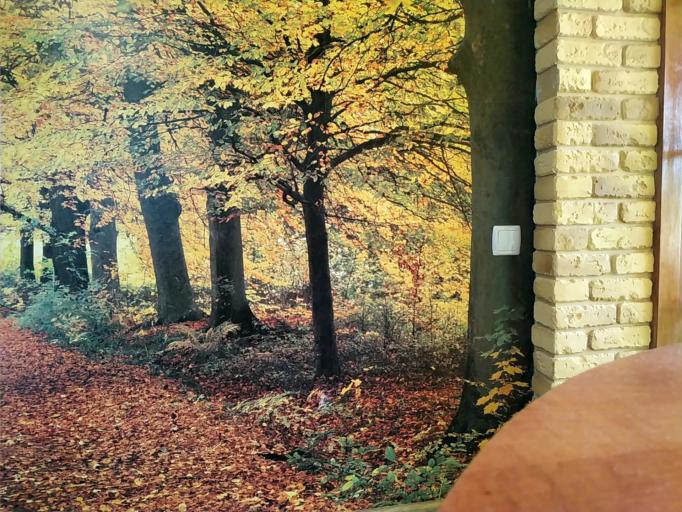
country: RU
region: Novgorod
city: Sol'tsy
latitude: 57.9058
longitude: 30.2127
